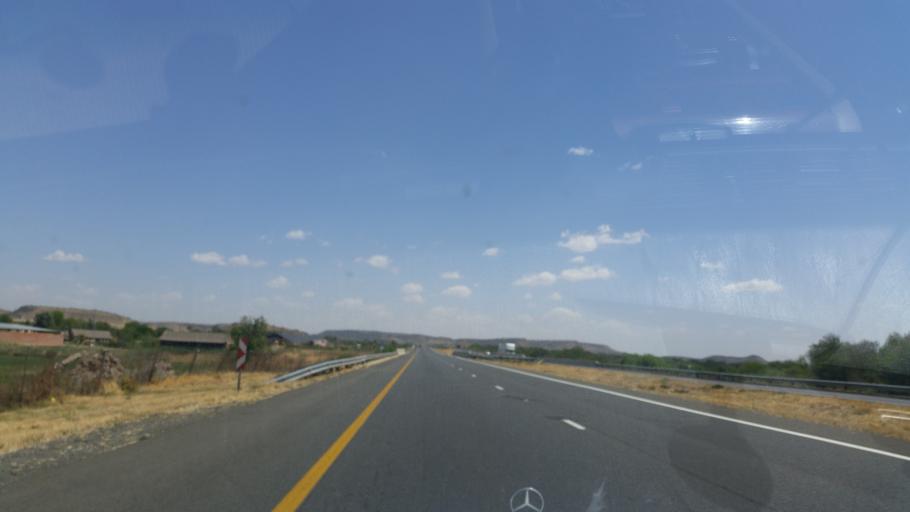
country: ZA
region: Orange Free State
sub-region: Mangaung Metropolitan Municipality
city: Bloemfontein
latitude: -28.9677
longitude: 26.3367
